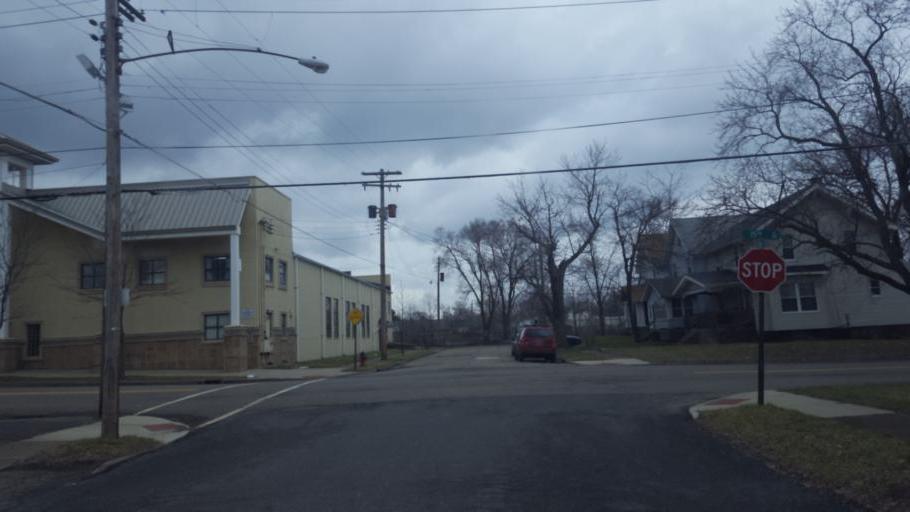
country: US
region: Ohio
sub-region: Stark County
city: Canton
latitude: 40.7835
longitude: -81.4010
